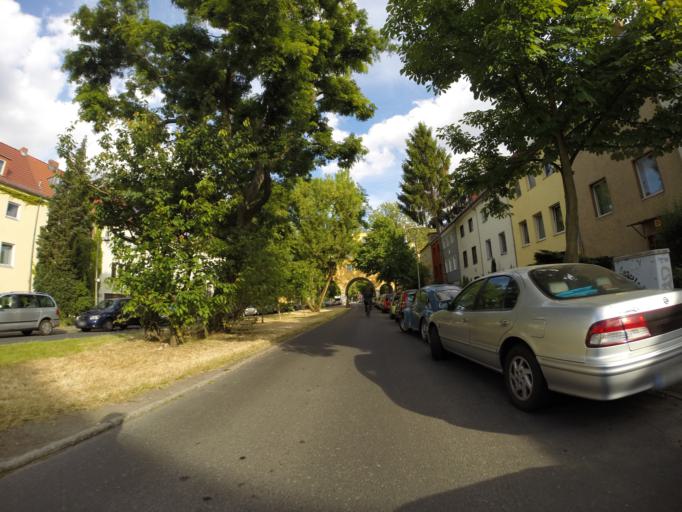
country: DE
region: Berlin
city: Tempelhof Bezirk
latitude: 52.4731
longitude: 13.3836
